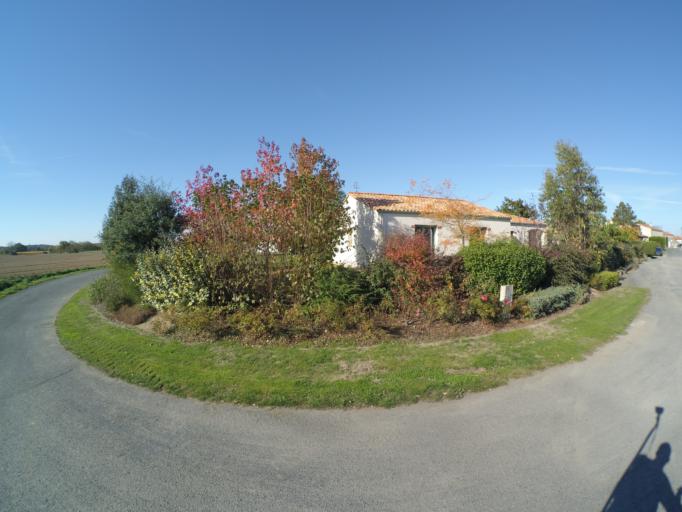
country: FR
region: Pays de la Loire
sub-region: Departement de la Loire-Atlantique
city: Saint-Lumine-de-Clisson
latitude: 47.0714
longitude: -1.3281
